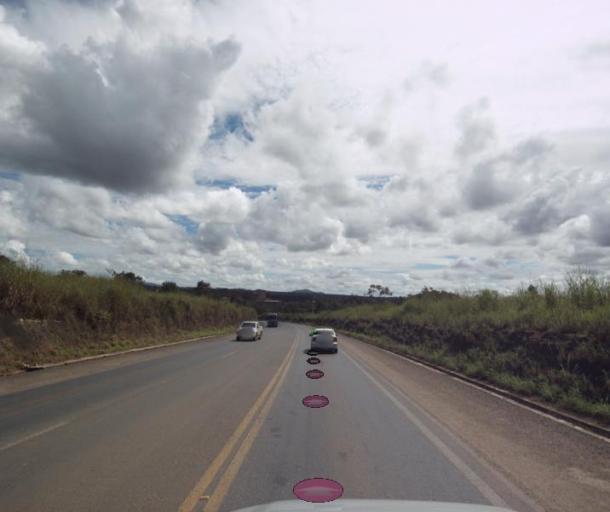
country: BR
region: Goias
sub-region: Uruacu
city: Uruacu
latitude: -14.5094
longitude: -49.1482
